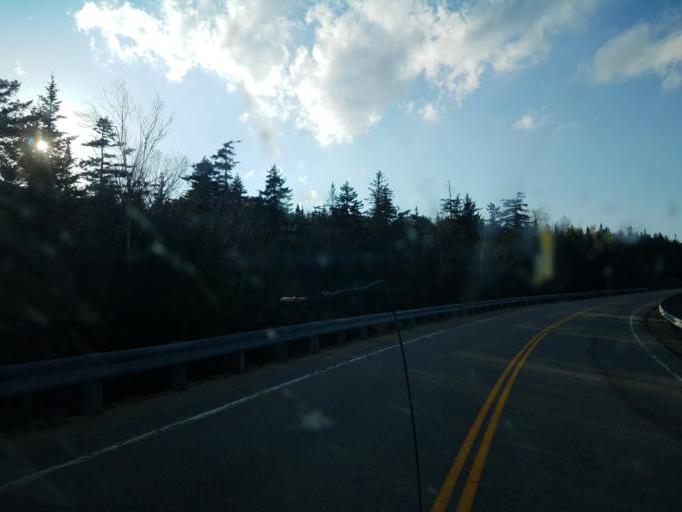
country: US
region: New Hampshire
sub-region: Grafton County
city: Woodstock
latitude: 44.0217
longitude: -71.4922
